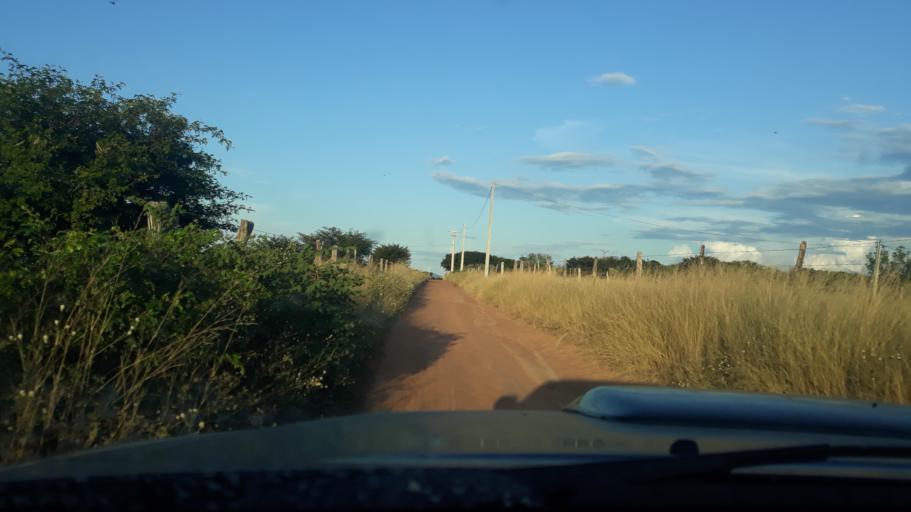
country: BR
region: Bahia
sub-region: Riacho De Santana
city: Riacho de Santana
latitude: -13.8545
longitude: -43.0550
